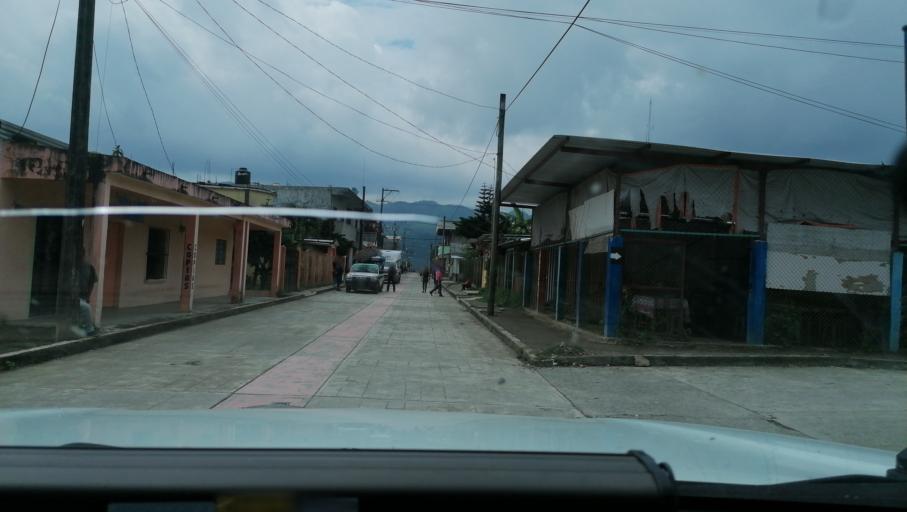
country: MX
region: Chiapas
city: Ixtacomitan
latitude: 17.3390
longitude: -93.1301
